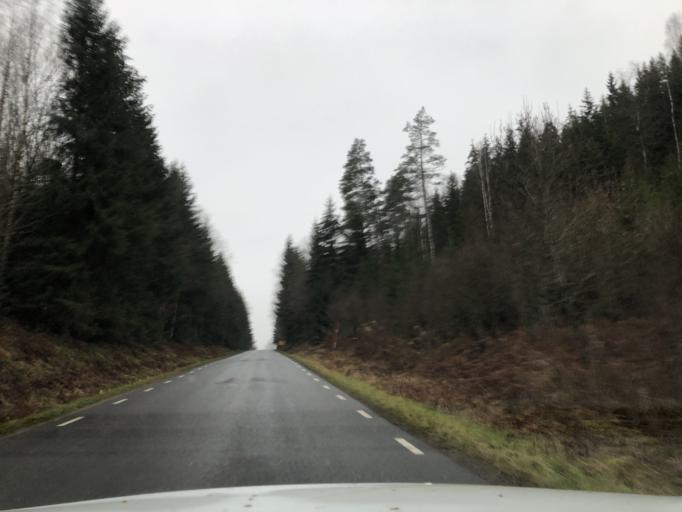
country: SE
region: Vaestra Goetaland
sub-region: Ulricehamns Kommun
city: Ulricehamn
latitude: 57.8327
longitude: 13.3985
